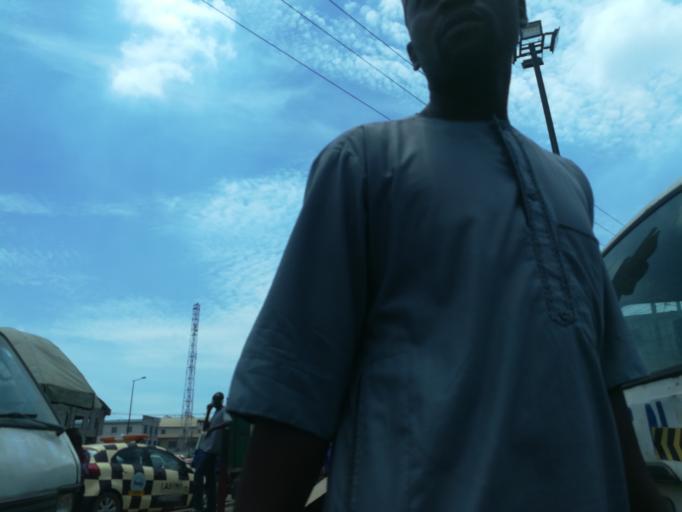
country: NG
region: Lagos
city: Ikorodu
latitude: 6.6206
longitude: 3.5033
